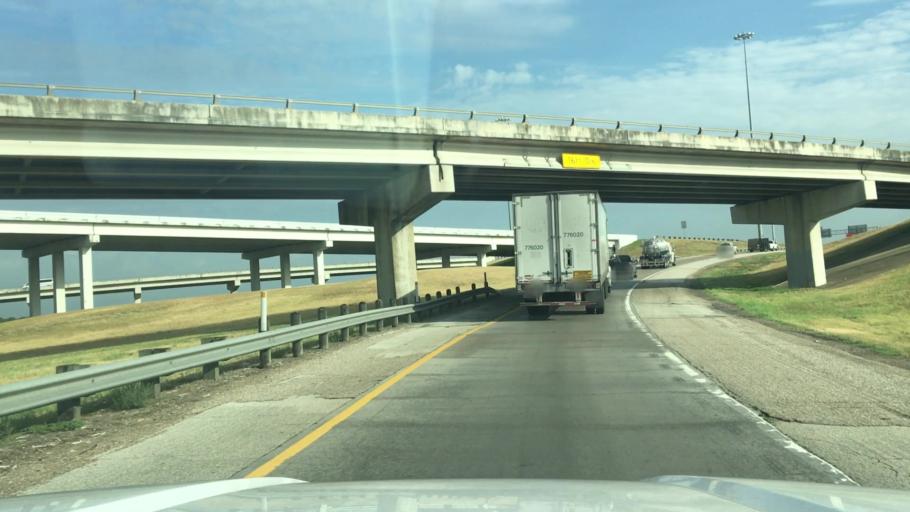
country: US
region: Texas
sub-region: Dallas County
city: Duncanville
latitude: 32.6723
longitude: -96.9458
